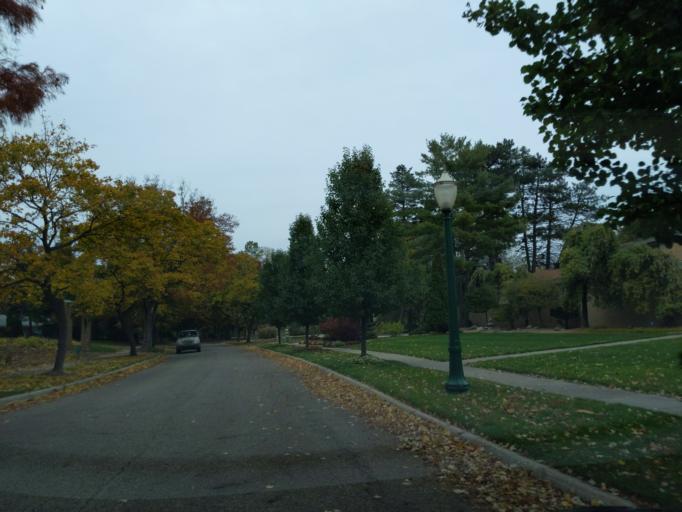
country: US
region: Michigan
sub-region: Ingham County
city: Edgemont Park
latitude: 42.7190
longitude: -84.5841
